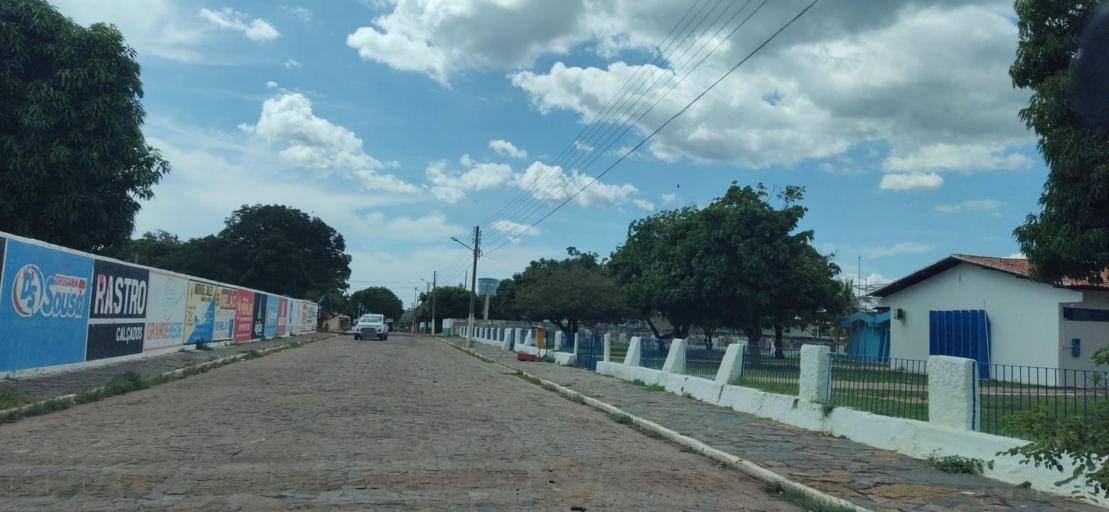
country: BR
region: Piaui
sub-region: Valenca Do Piaui
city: Valenca do Piaui
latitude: -6.4024
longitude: -41.7344
